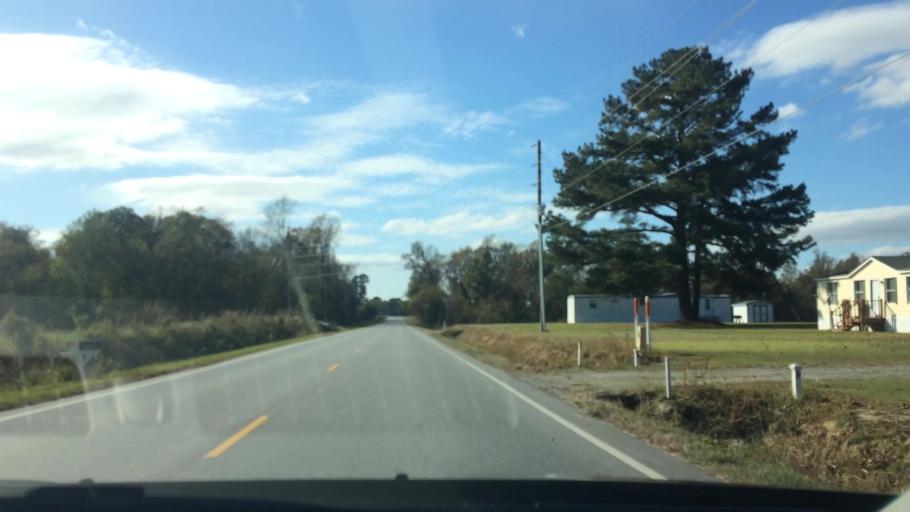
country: US
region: North Carolina
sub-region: Greene County
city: Maury
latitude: 35.4697
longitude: -77.5331
